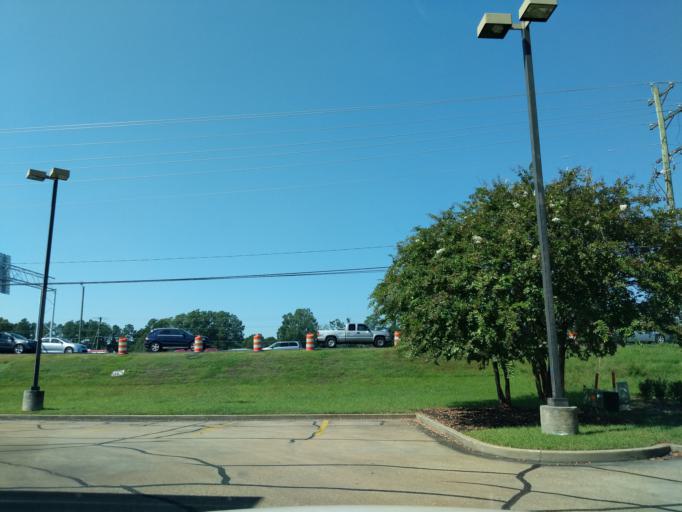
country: US
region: Alabama
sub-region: Montgomery County
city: Pike Road
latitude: 32.3587
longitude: -86.1706
